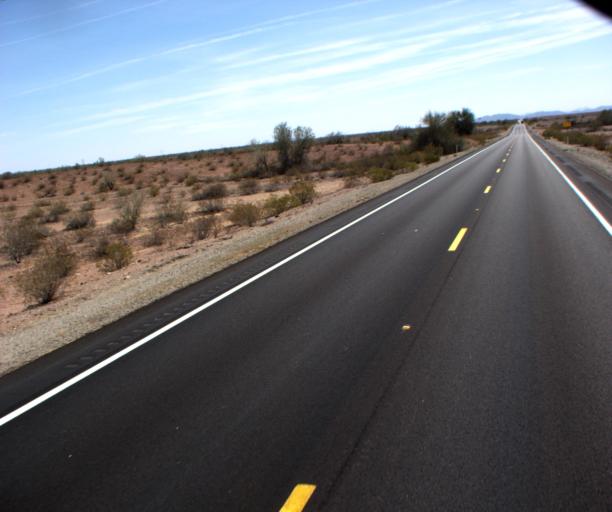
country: US
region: Arizona
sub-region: Yuma County
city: Wellton
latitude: 33.0518
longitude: -114.2914
